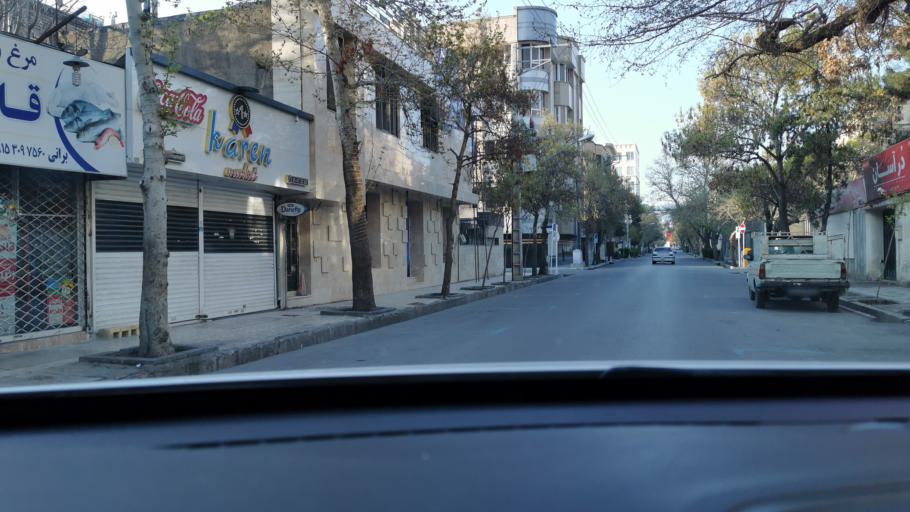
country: IR
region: Razavi Khorasan
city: Mashhad
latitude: 36.2987
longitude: 59.5803
